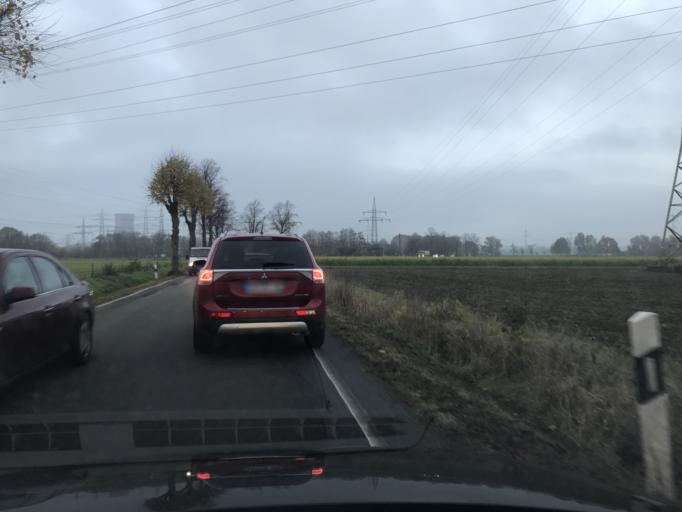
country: DE
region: North Rhine-Westphalia
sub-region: Regierungsbezirk Arnsberg
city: Welver
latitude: 51.6689
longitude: 7.9840
